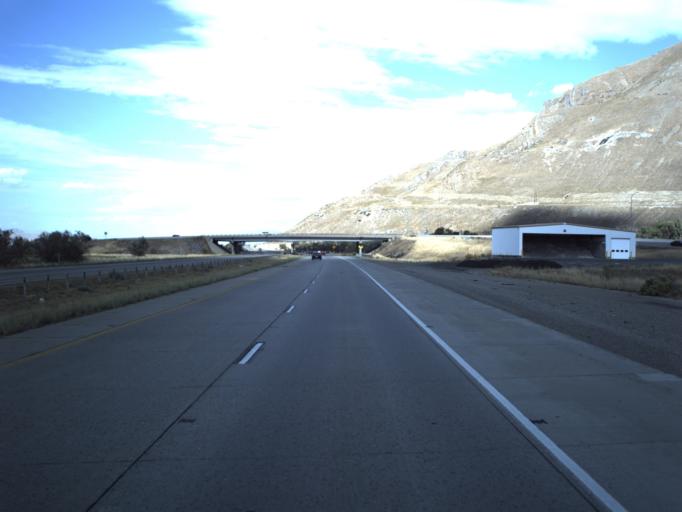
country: US
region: Utah
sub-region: Tooele County
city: Stansbury park
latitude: 40.6912
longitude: -112.2657
